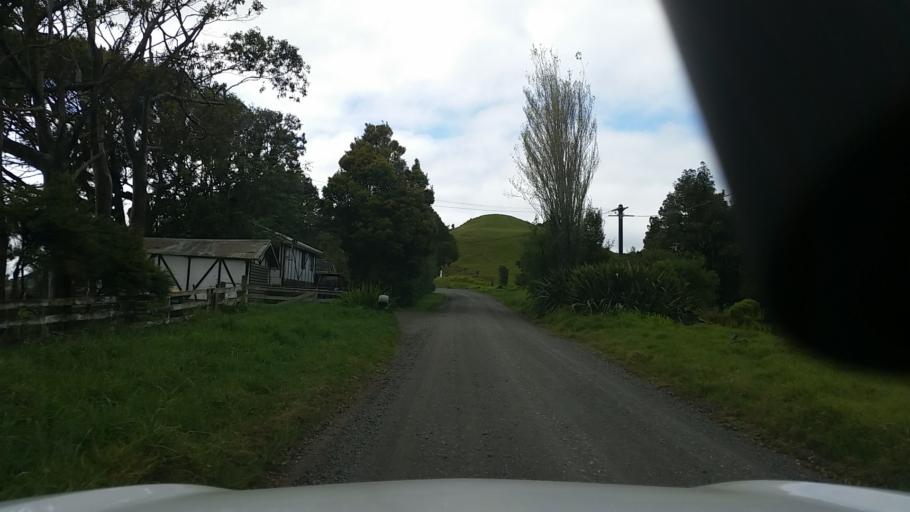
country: NZ
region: Auckland
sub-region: Auckland
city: Muriwai Beach
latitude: -36.8488
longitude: 174.4802
